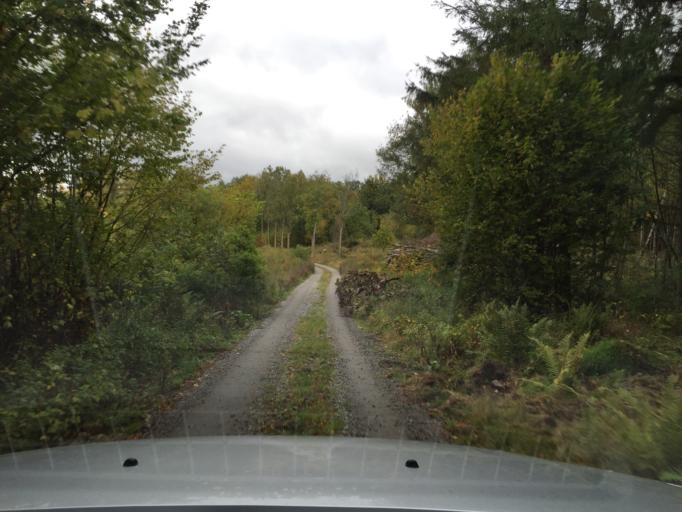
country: SE
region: Skane
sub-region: Hassleholms Kommun
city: Tormestorp
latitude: 56.0647
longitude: 13.7538
